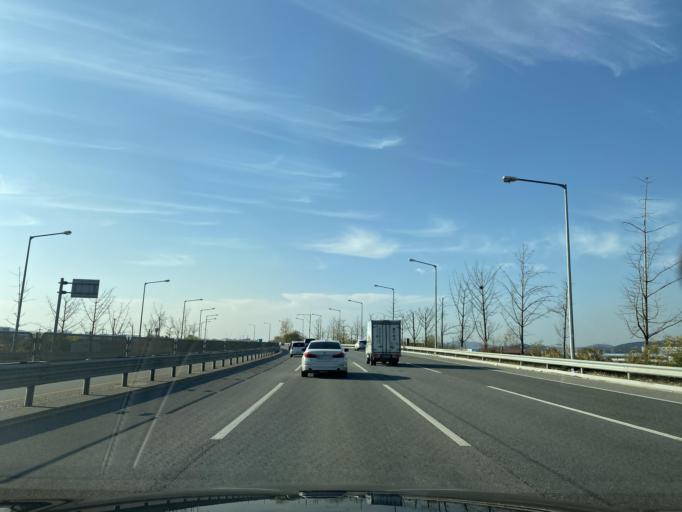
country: KR
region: Chungcheongnam-do
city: Asan
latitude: 36.7790
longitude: 127.0678
